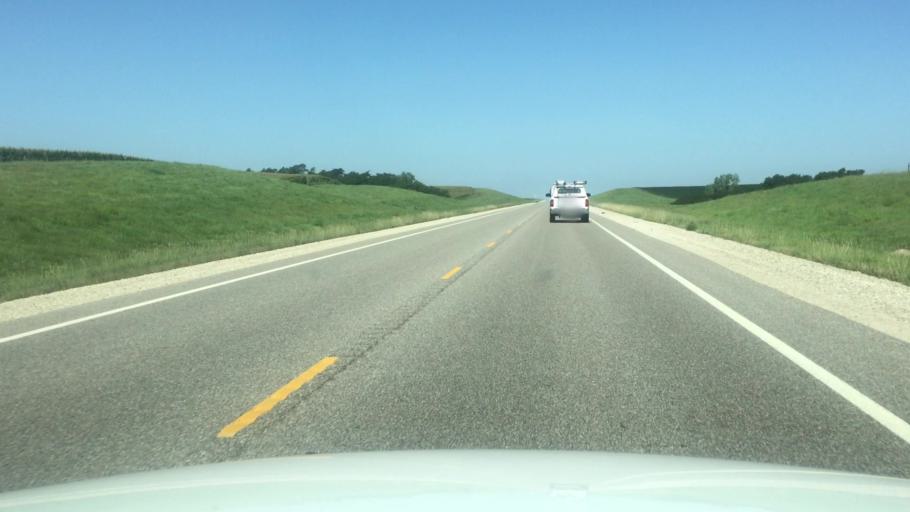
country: US
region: Kansas
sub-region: Doniphan County
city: Troy
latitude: 39.7991
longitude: -95.1642
